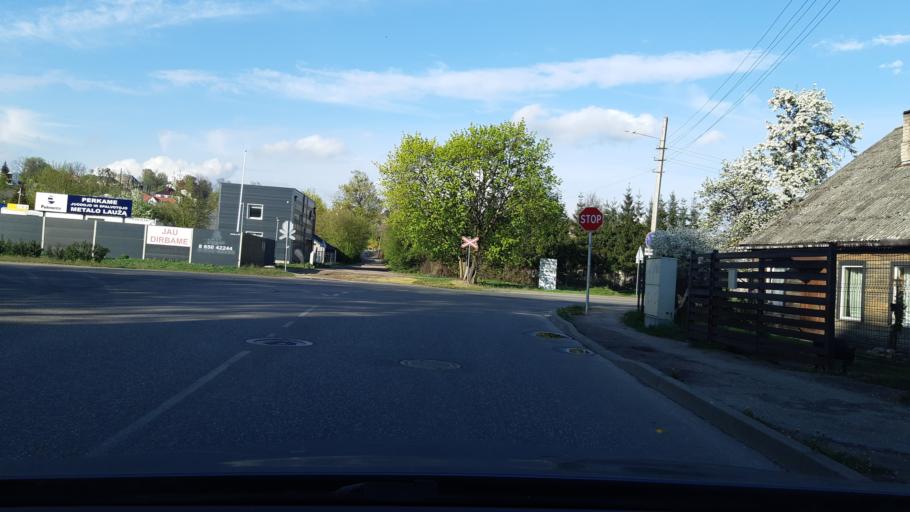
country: LT
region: Kauno apskritis
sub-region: Kaunas
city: Aleksotas
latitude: 54.8710
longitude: 23.9439
